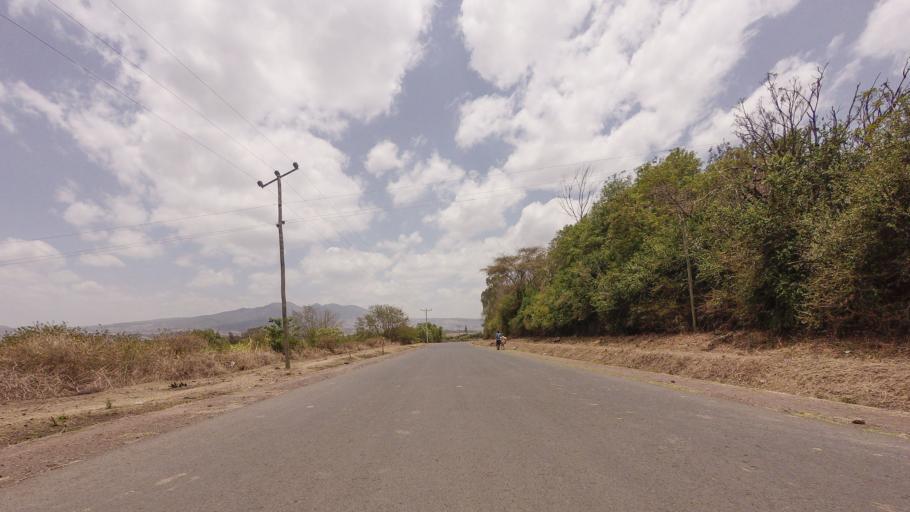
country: ET
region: Oromiya
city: Bishoftu
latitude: 8.7883
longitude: 38.9868
